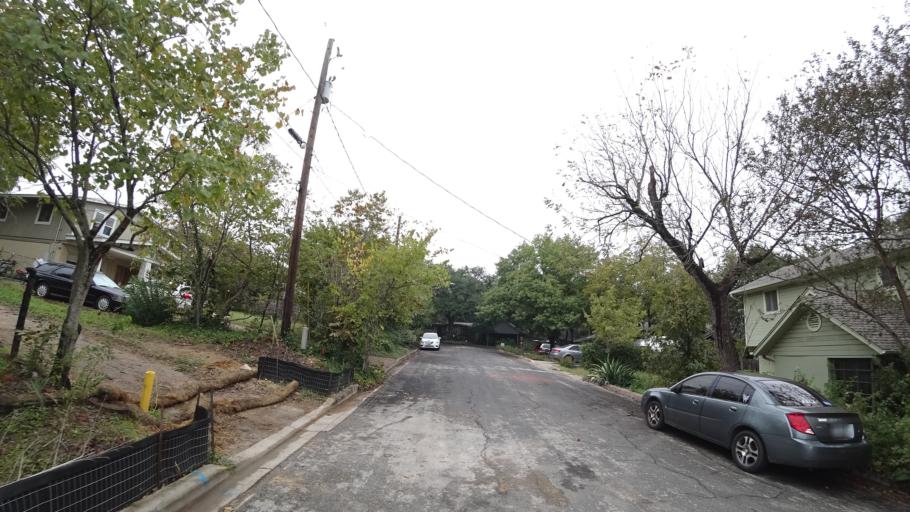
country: US
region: Texas
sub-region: Travis County
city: Rollingwood
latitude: 30.2568
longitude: -97.7730
